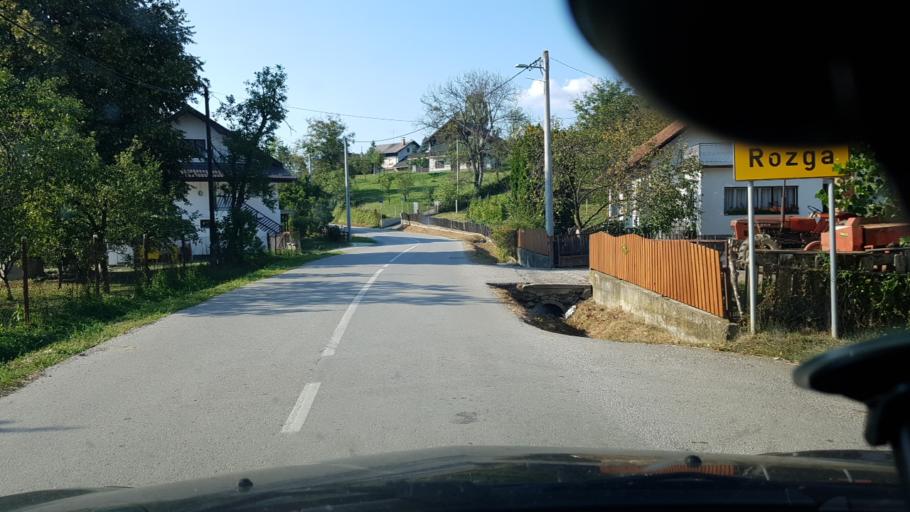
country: HR
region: Zagrebacka
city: Pojatno
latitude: 45.9412
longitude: 15.7299
